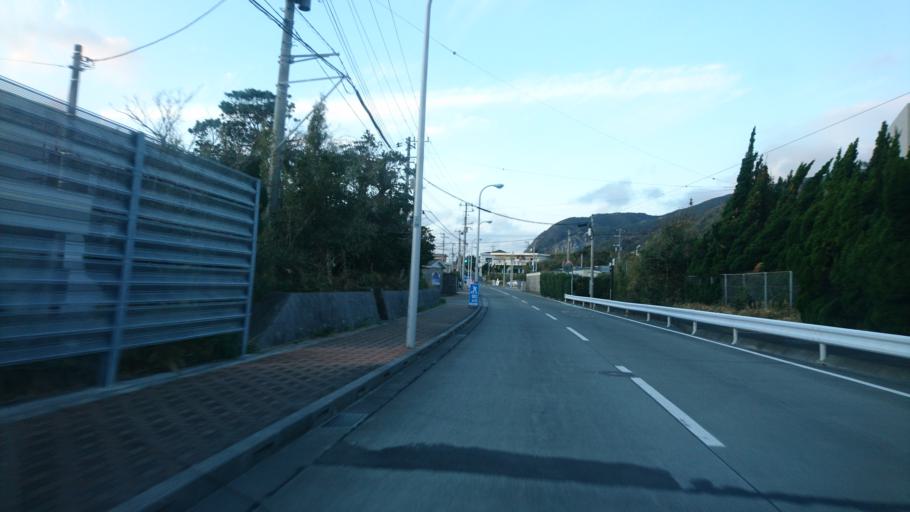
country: JP
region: Shizuoka
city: Shimoda
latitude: 34.3716
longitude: 139.2590
